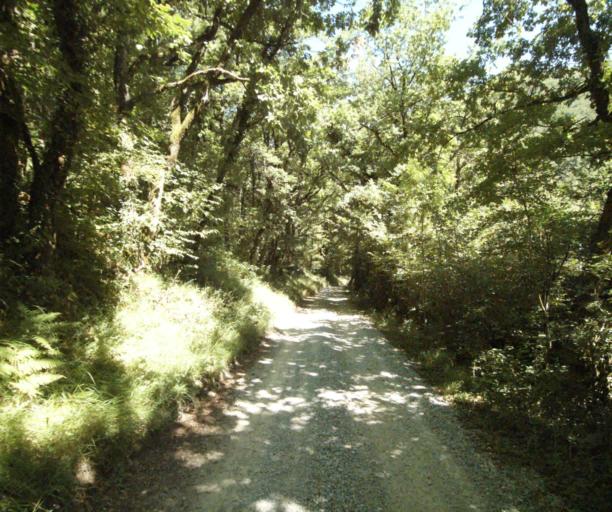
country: FR
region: Midi-Pyrenees
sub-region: Departement du Tarn
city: Soreze
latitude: 43.4391
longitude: 2.0926
